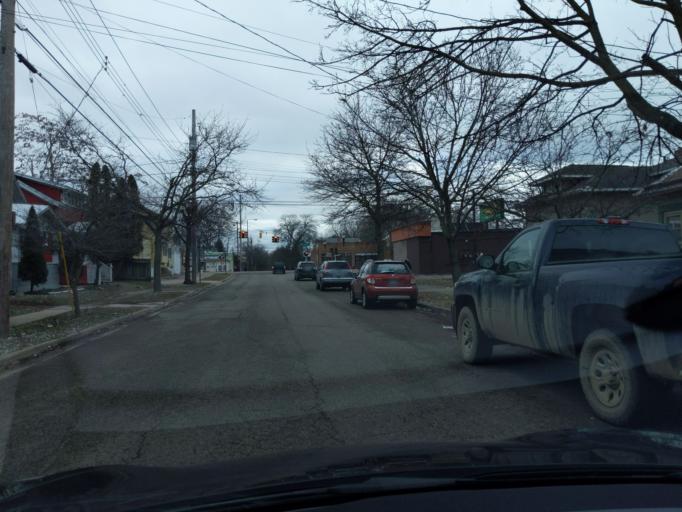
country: US
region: Michigan
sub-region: Ingham County
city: East Lansing
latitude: 42.7344
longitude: -84.5176
